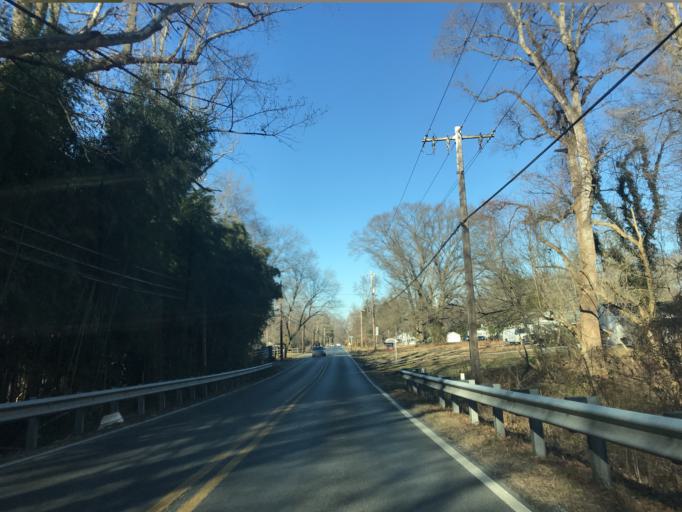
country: US
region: Maryland
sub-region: Prince George's County
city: Accokeek
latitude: 38.6805
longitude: -76.9861
